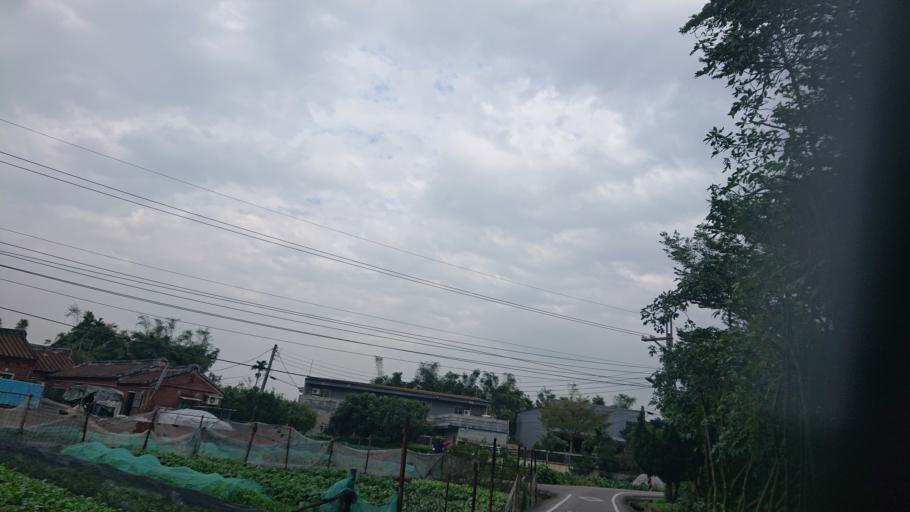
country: TW
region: Taiwan
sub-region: Taoyuan
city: Taoyuan
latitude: 24.9533
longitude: 121.3720
